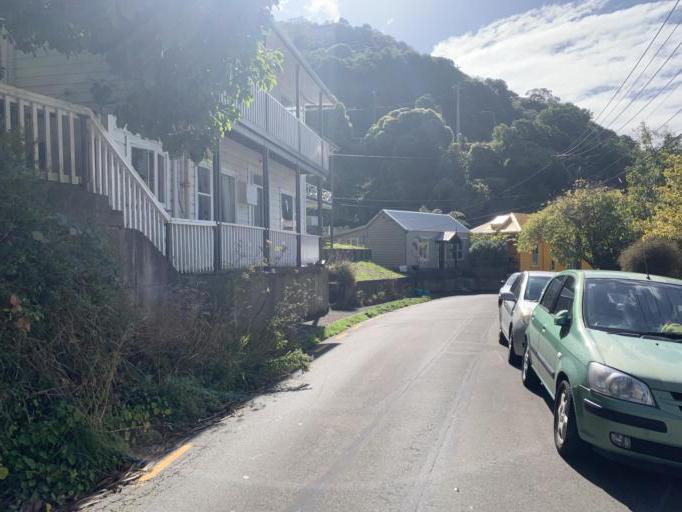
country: NZ
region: Wellington
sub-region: Wellington City
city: Kelburn
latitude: -41.2947
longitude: 174.7587
